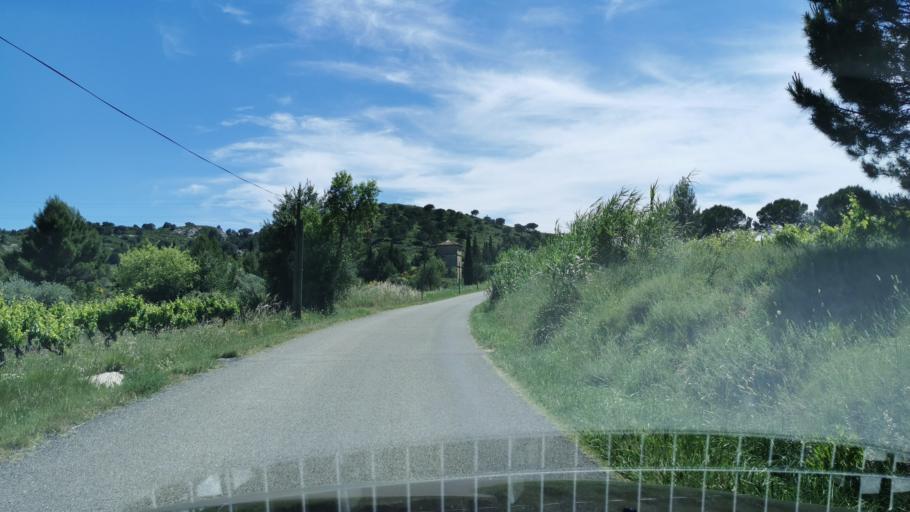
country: FR
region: Languedoc-Roussillon
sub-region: Departement de l'Aude
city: Nevian
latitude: 43.2042
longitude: 2.9034
